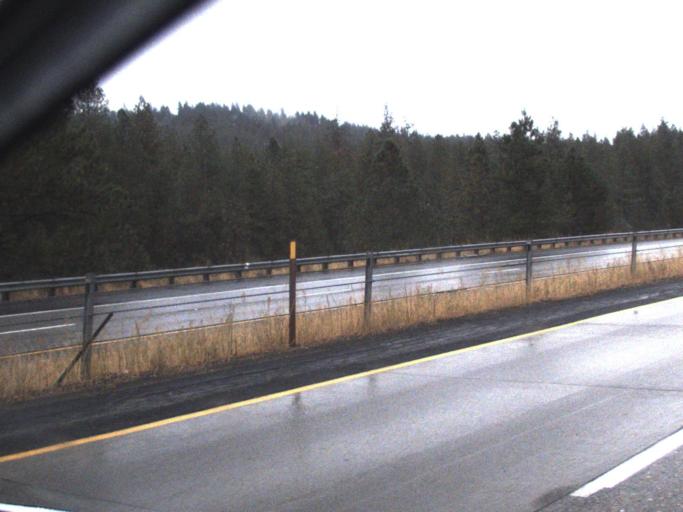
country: US
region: Washington
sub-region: Spokane County
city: Spokane
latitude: 47.5983
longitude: -117.4081
